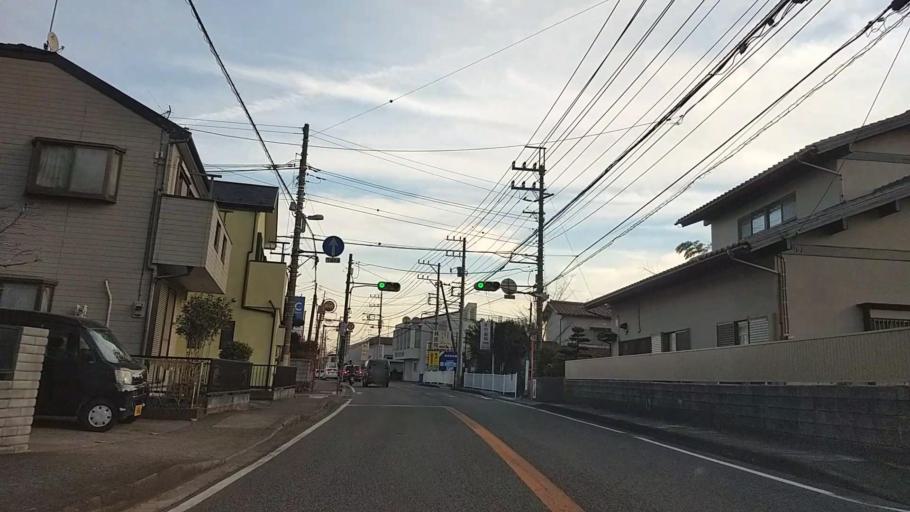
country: JP
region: Kanagawa
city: Atsugi
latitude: 35.4804
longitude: 139.3375
